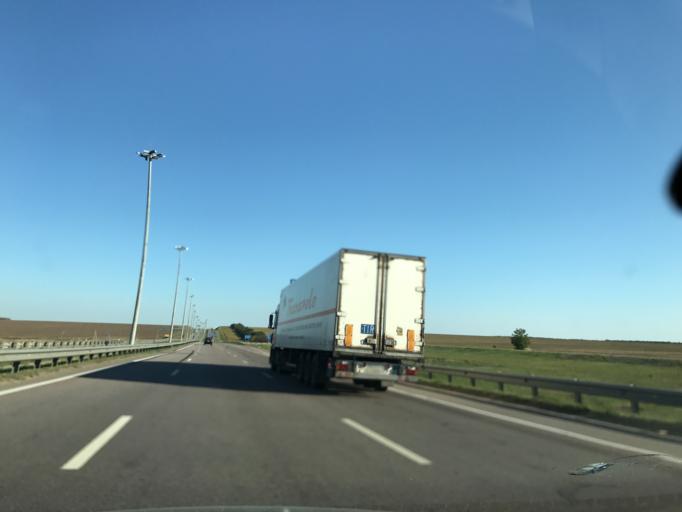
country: RU
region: Rostov
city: Glubokiy
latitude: 48.4503
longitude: 40.3408
